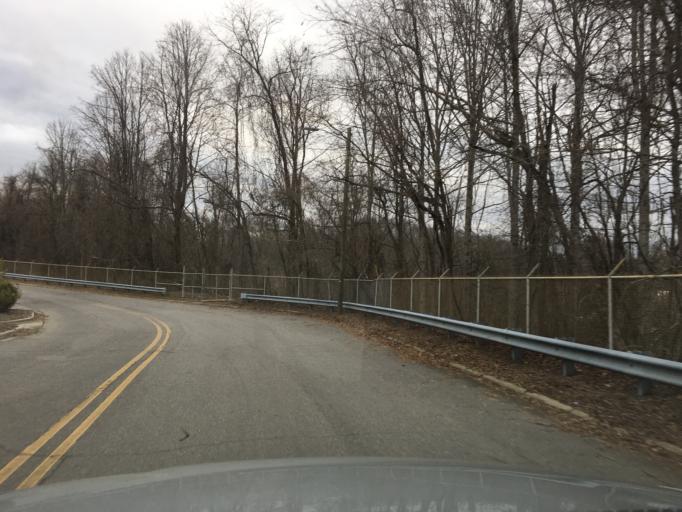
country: US
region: North Carolina
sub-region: Buncombe County
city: Woodfin
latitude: 35.6076
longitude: -82.5830
